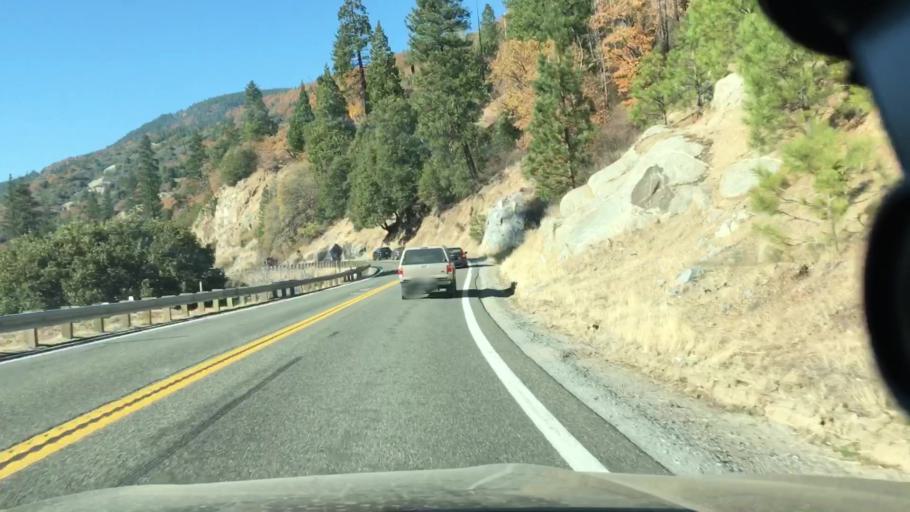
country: US
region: California
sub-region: El Dorado County
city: Pollock Pines
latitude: 38.7717
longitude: -120.3874
